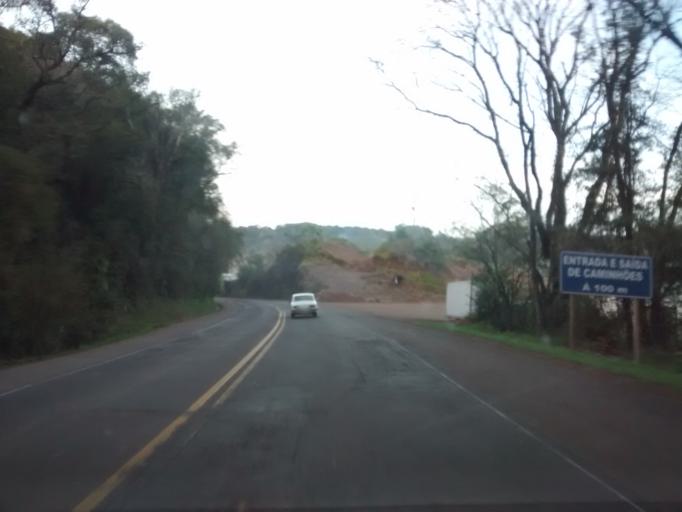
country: BR
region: Parana
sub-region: Francisco Beltrao
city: Francisco Beltrao
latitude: -26.1082
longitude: -53.0568
